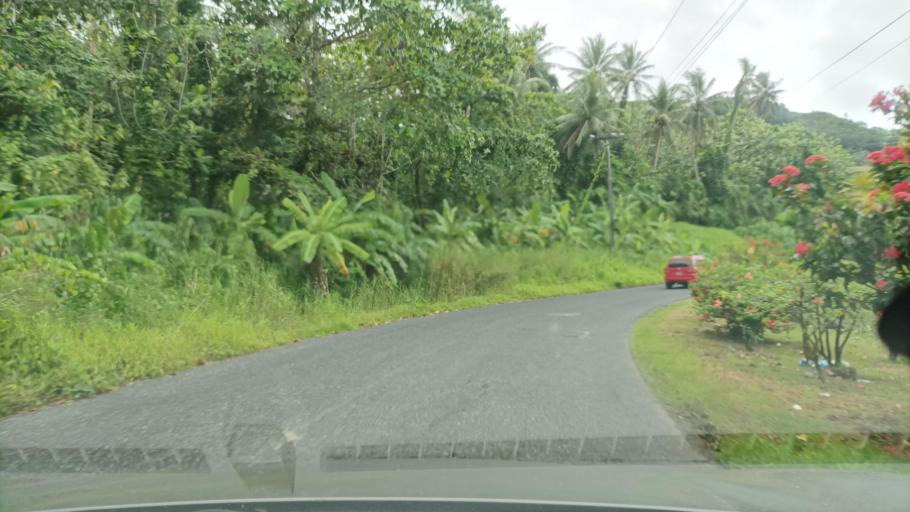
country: FM
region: Pohnpei
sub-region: Kolonia Municipality
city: Kolonia
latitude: 6.9625
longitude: 158.2621
